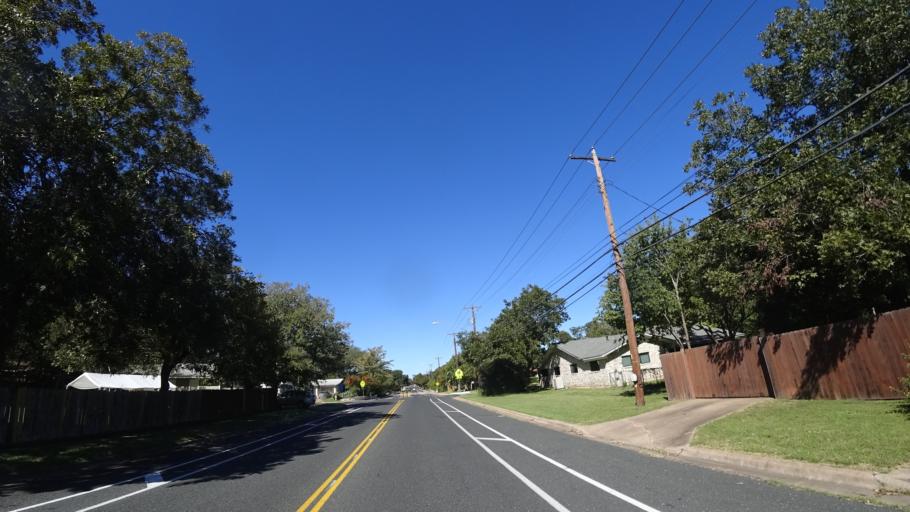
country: US
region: Texas
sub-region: Travis County
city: Rollingwood
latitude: 30.2228
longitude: -97.7981
